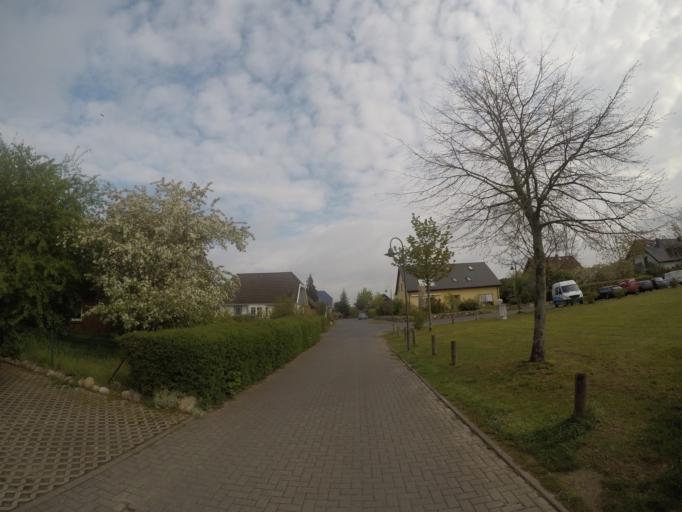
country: DE
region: Mecklenburg-Vorpommern
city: Papendorf
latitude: 54.0517
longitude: 12.1345
